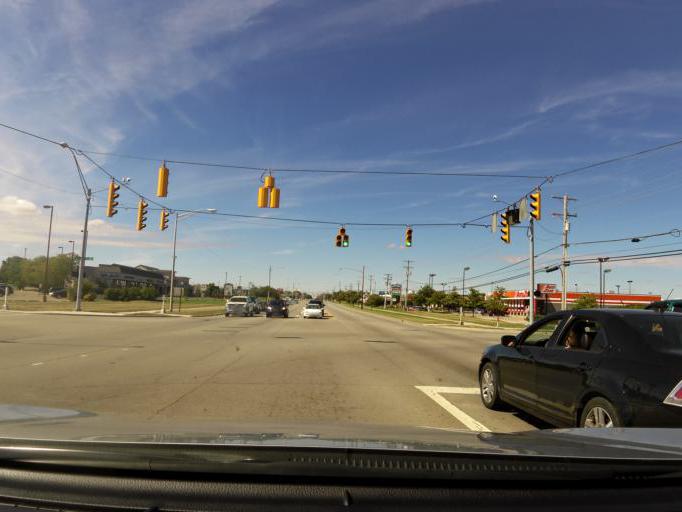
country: US
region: Ohio
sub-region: Miami County
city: Troy
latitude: 40.0542
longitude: -84.2365
